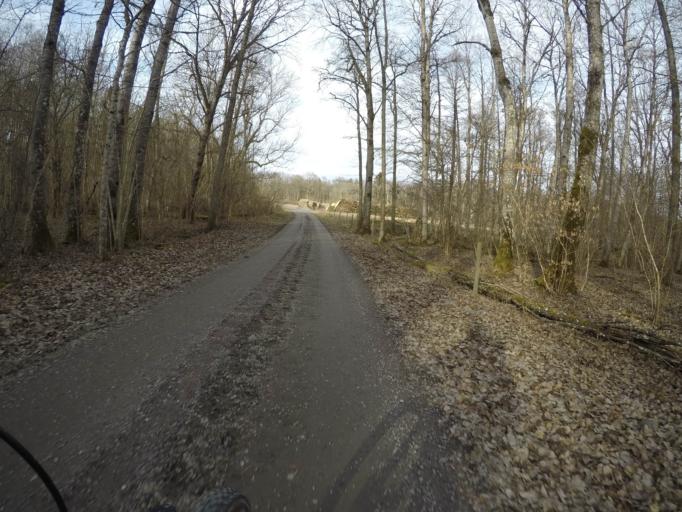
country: SE
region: Soedermanland
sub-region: Eskilstuna Kommun
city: Hallbybrunn
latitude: 59.4505
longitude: 16.3982
